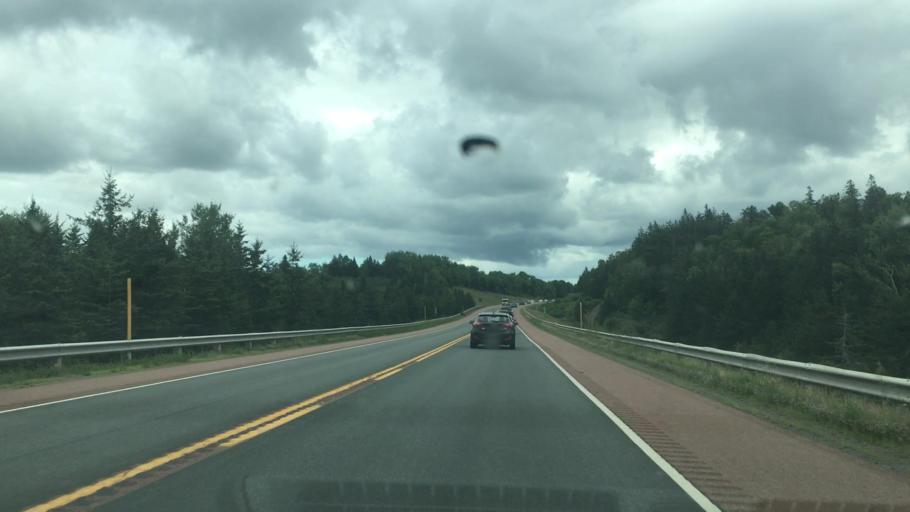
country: CA
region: Nova Scotia
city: Antigonish
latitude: 45.5941
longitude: -62.0604
